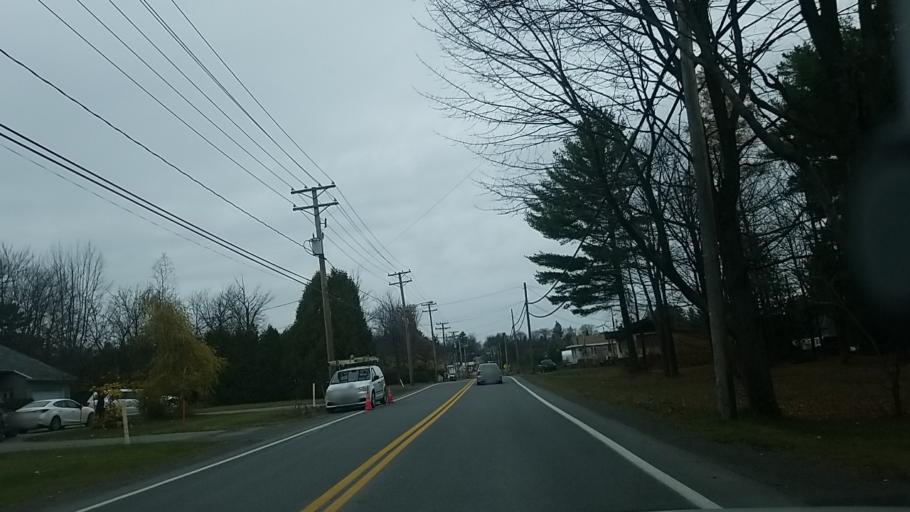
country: CA
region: Quebec
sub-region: Laurentides
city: Saint-Jerome
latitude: 45.7862
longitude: -74.0526
